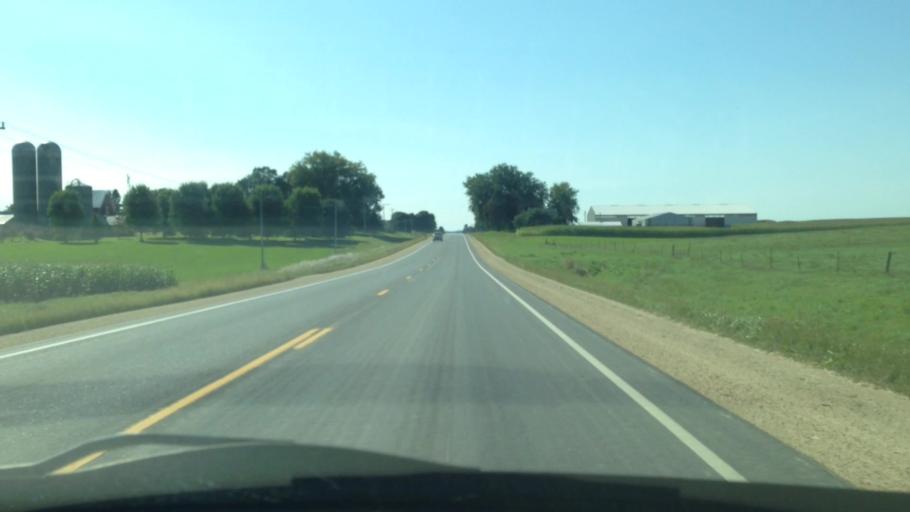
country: US
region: Minnesota
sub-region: Winona County
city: Lewiston
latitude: 43.9697
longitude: -91.8311
